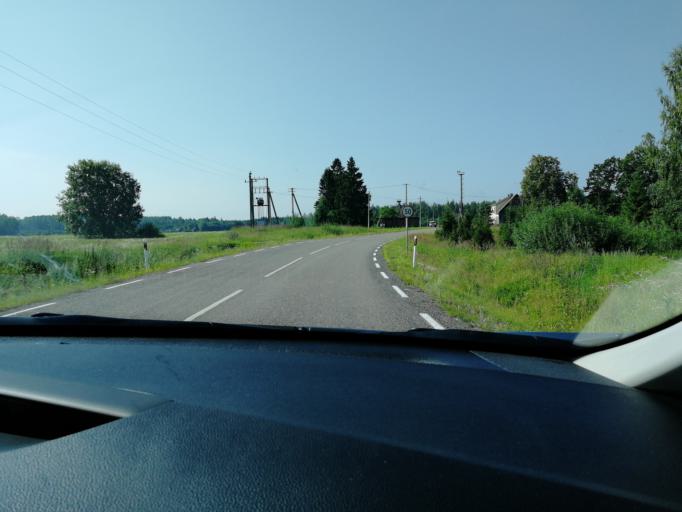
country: EE
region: Paernumaa
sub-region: Saarde vald
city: Kilingi-Nomme
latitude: 58.0224
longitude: 25.0089
